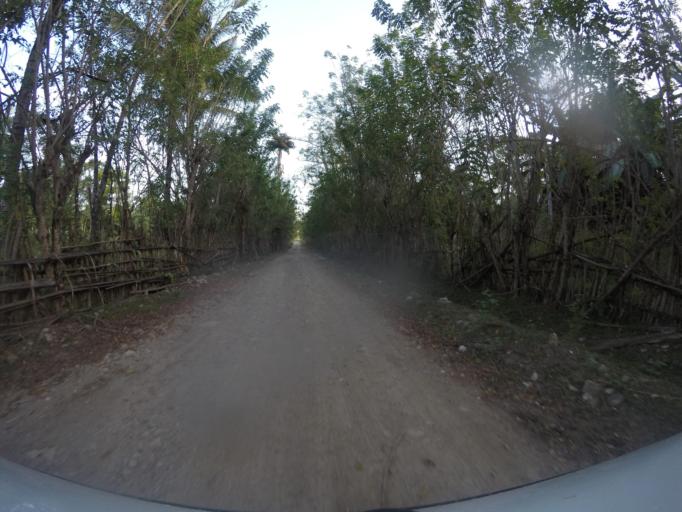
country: TL
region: Baucau
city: Venilale
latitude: -8.7255
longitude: 126.7087
